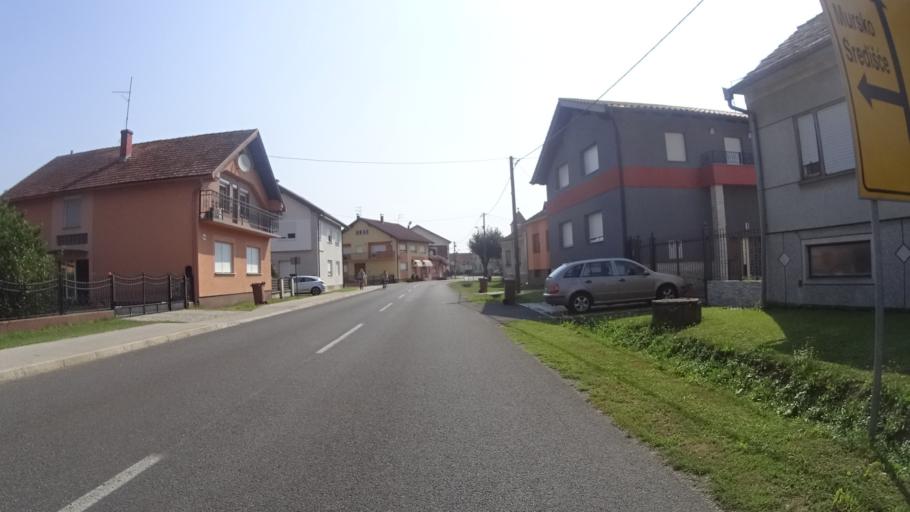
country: HR
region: Medimurska
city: Domasinec
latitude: 46.3949
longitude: 16.5919
